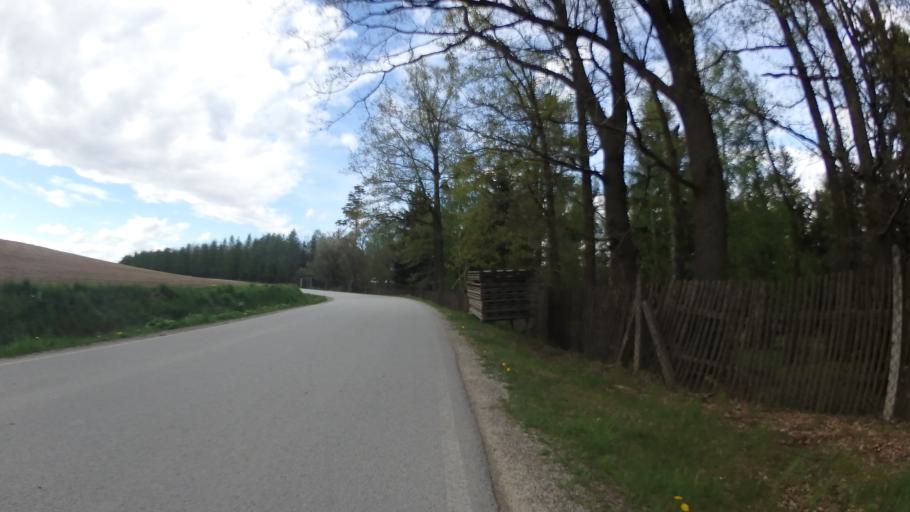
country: CZ
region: Vysocina
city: Merin
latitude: 49.3677
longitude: 15.8996
